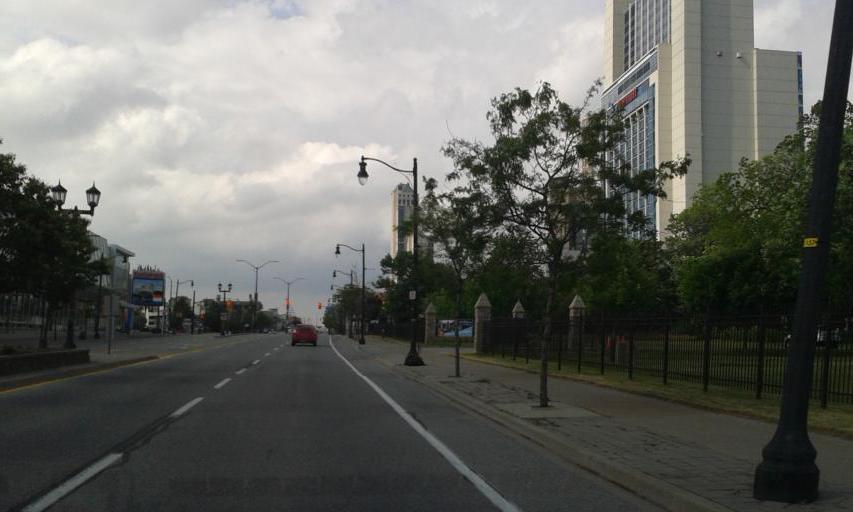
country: CA
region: Ontario
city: Niagara Falls
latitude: 43.0754
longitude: -79.0836
